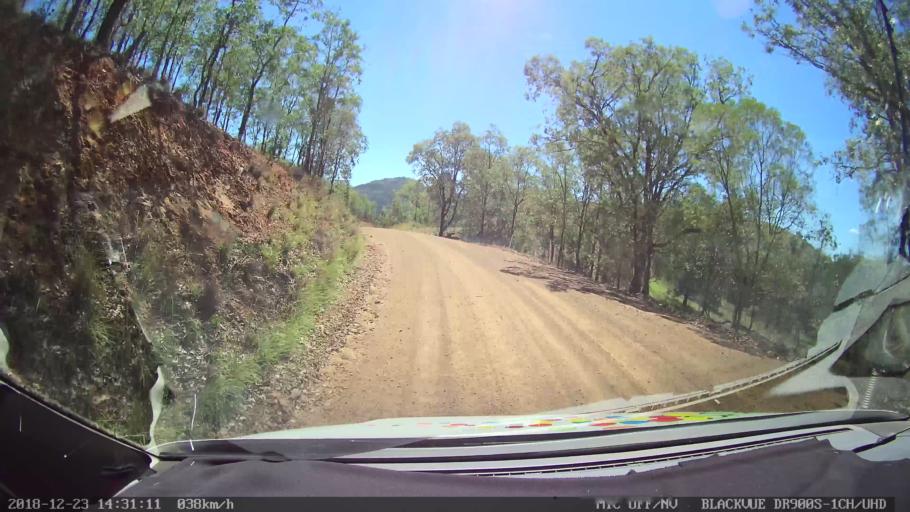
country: AU
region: New South Wales
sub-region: Tamworth Municipality
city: Manilla
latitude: -30.6027
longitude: 150.9281
